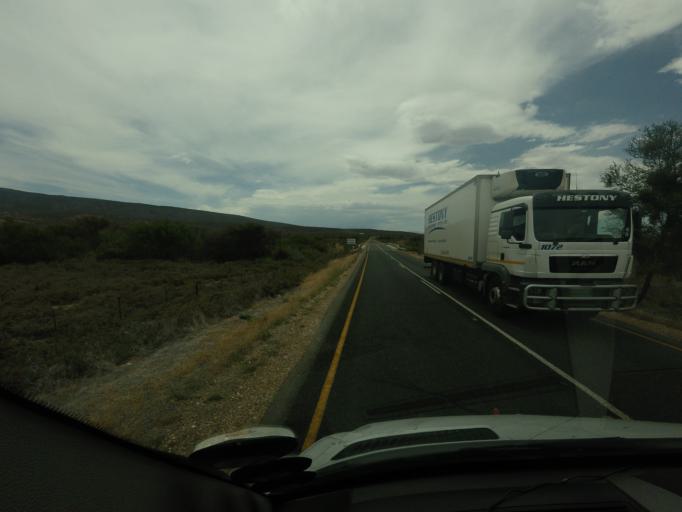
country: ZA
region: Western Cape
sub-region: Eden District Municipality
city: Riversdale
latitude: -33.8242
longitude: 20.8909
